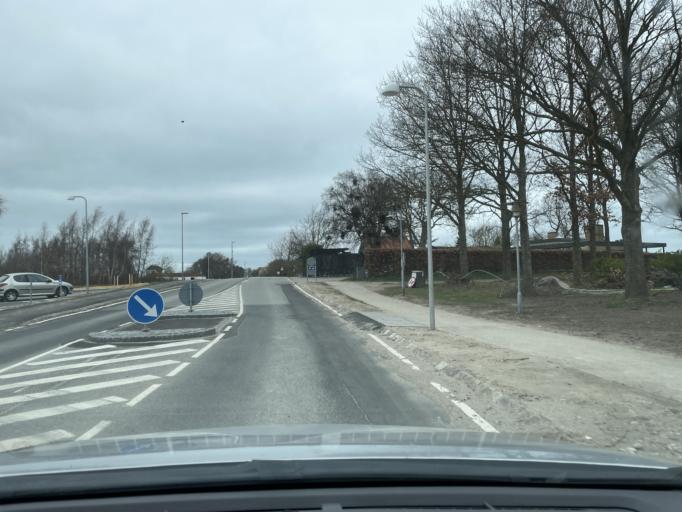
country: DK
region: South Denmark
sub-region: Nyborg Kommune
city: Nyborg
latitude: 55.3474
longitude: 10.7957
